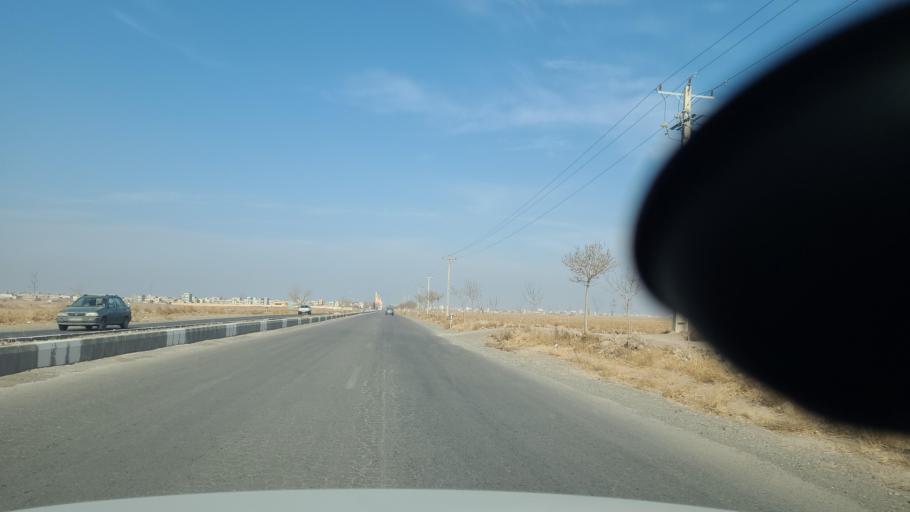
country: IR
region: Razavi Khorasan
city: Fariman
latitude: 35.6733
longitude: 59.8424
